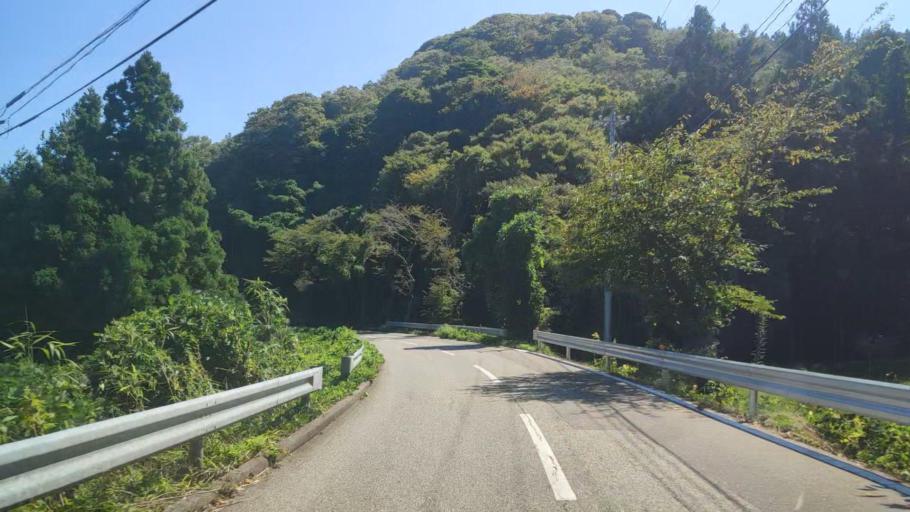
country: JP
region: Ishikawa
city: Nanao
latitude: 37.5292
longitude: 137.2762
